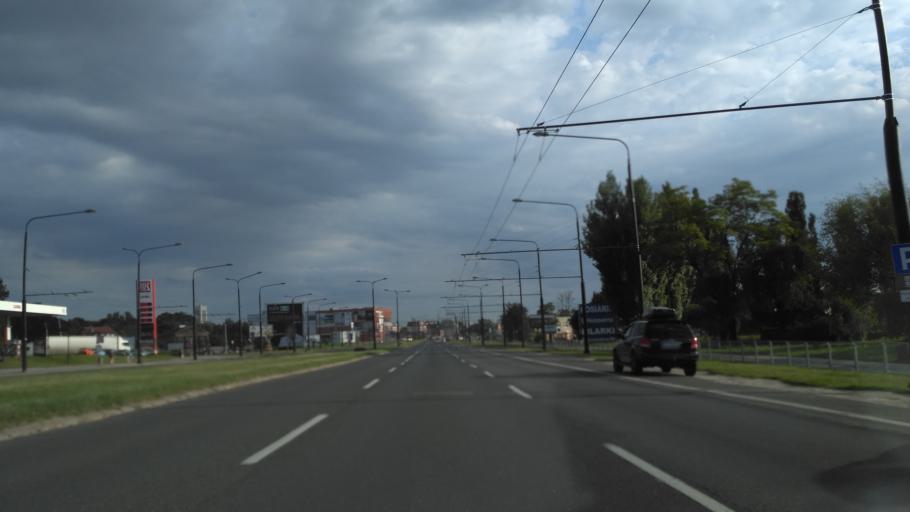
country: PL
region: Lublin Voivodeship
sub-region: Powiat lubelski
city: Lublin
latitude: 51.2443
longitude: 22.5733
